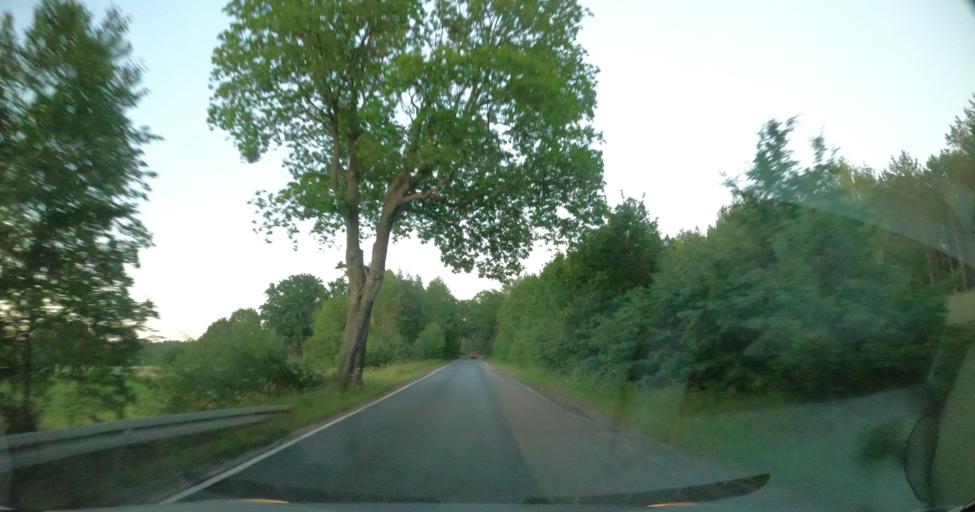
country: PL
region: Pomeranian Voivodeship
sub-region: Powiat wejherowski
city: Luzino
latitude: 54.4662
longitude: 18.1027
